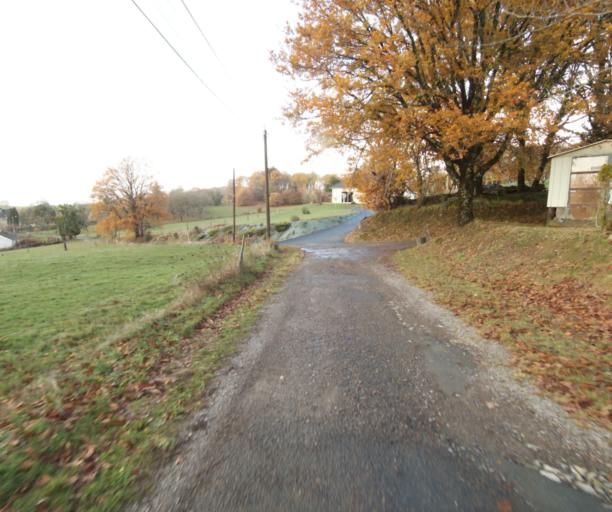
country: FR
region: Limousin
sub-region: Departement de la Correze
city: Cornil
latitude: 45.2188
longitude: 1.6762
